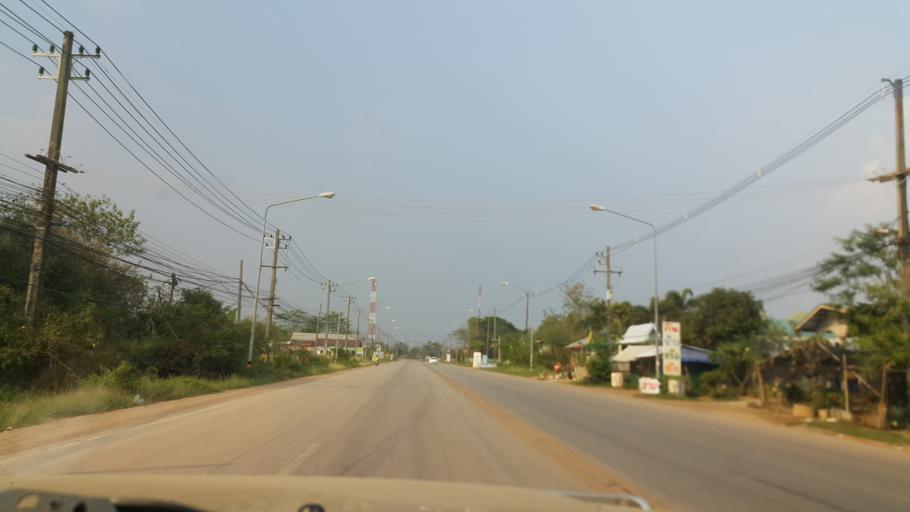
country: TH
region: Nakhon Phanom
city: That Phanom
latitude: 16.9506
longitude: 104.7219
